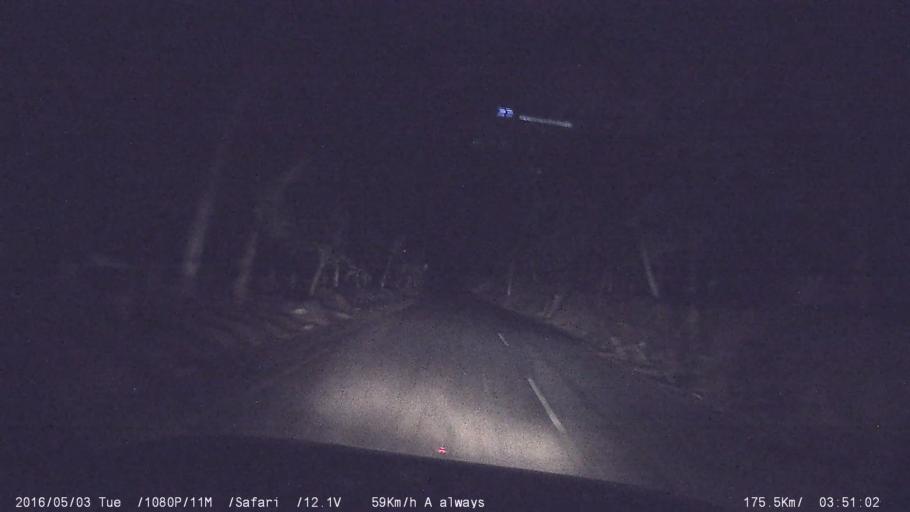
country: IN
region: Kerala
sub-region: Kottayam
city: Palackattumala
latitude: 9.8337
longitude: 76.6066
